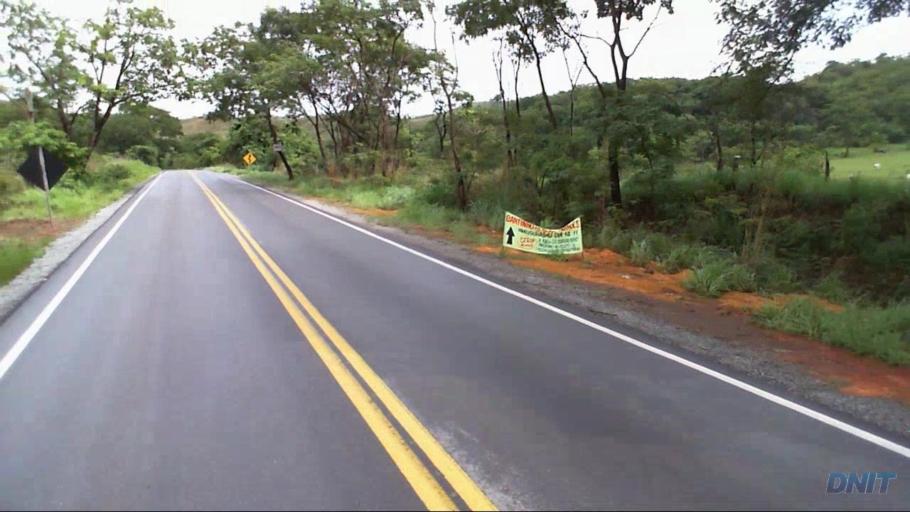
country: BR
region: Goias
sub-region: Padre Bernardo
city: Padre Bernardo
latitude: -15.4979
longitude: -48.2218
